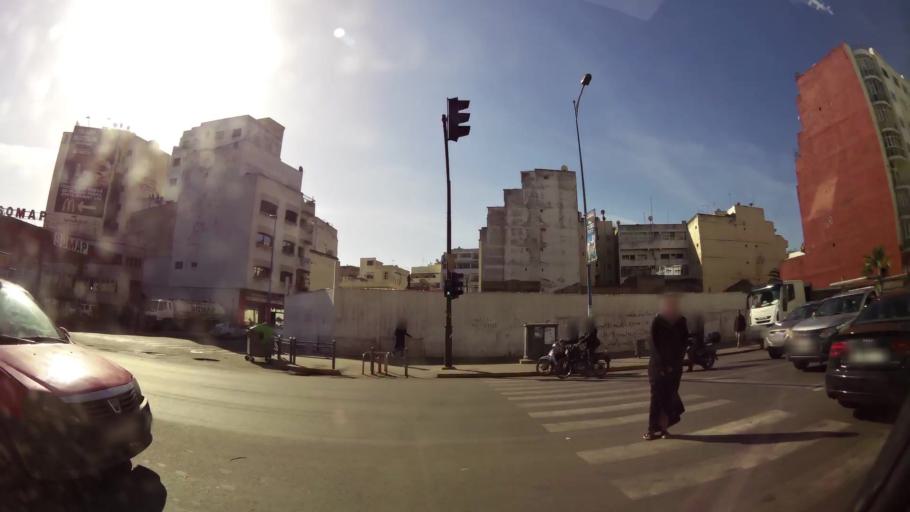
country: MA
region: Grand Casablanca
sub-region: Casablanca
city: Casablanca
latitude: 33.5971
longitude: -7.5920
